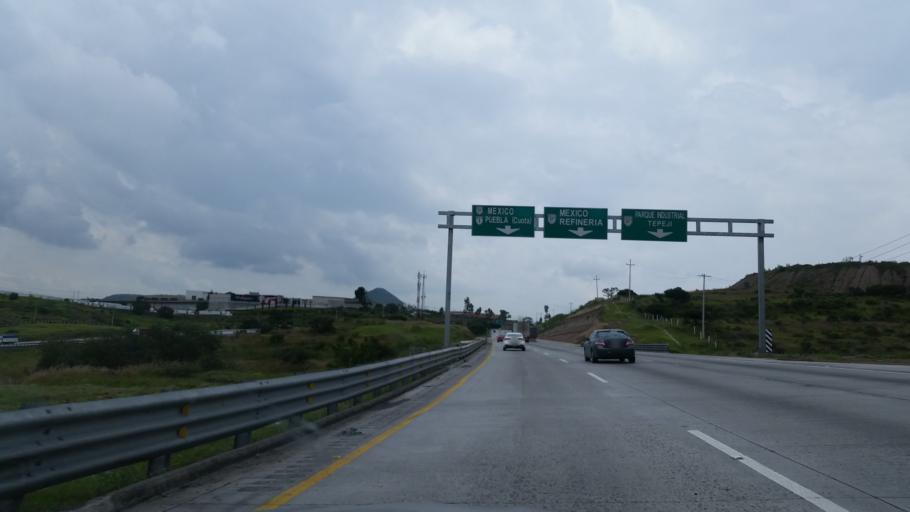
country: MX
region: Hidalgo
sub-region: Tepeji del Rio de Ocampo
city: Cantera de Villagran
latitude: 19.8556
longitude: -99.2965
